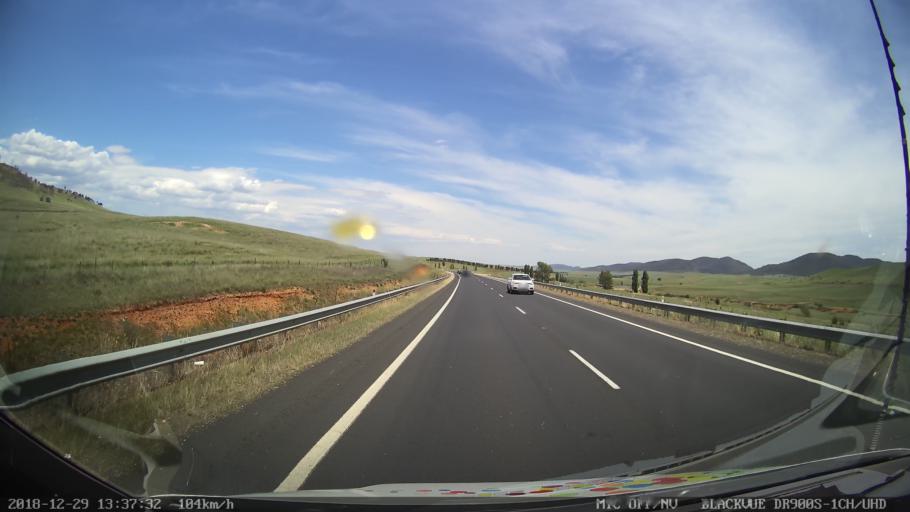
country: AU
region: New South Wales
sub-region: Cooma-Monaro
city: Cooma
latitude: -35.9853
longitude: 149.1371
